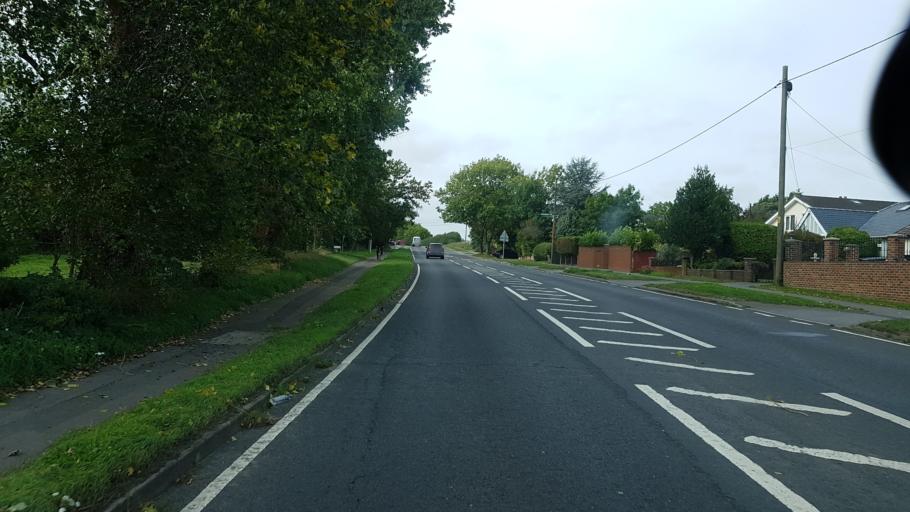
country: GB
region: England
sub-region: Kent
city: West Malling
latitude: 51.3019
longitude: 0.3979
